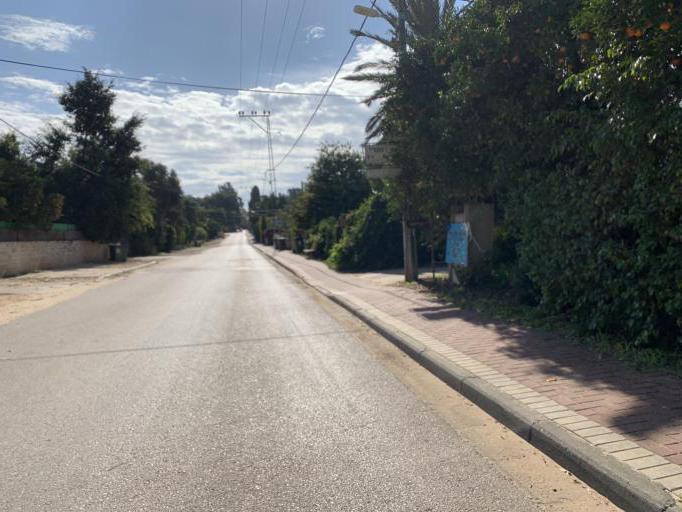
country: IL
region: Central District
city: Ra'anana
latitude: 32.1703
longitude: 34.8754
